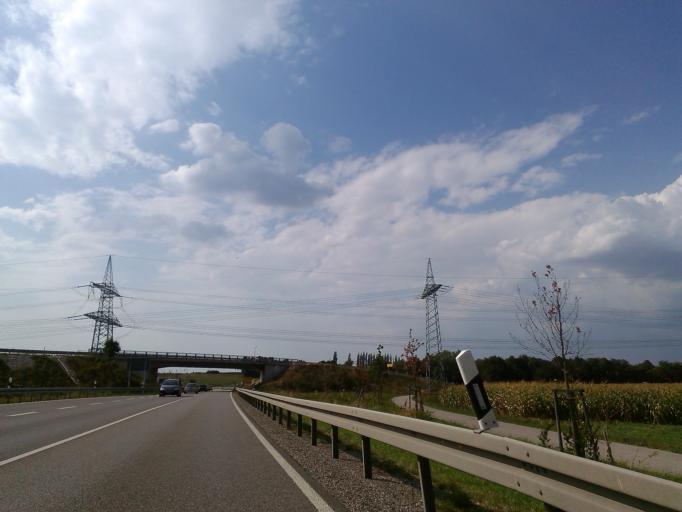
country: DE
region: Bavaria
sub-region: Upper Bavaria
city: Puchheim
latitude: 48.1437
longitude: 11.3543
